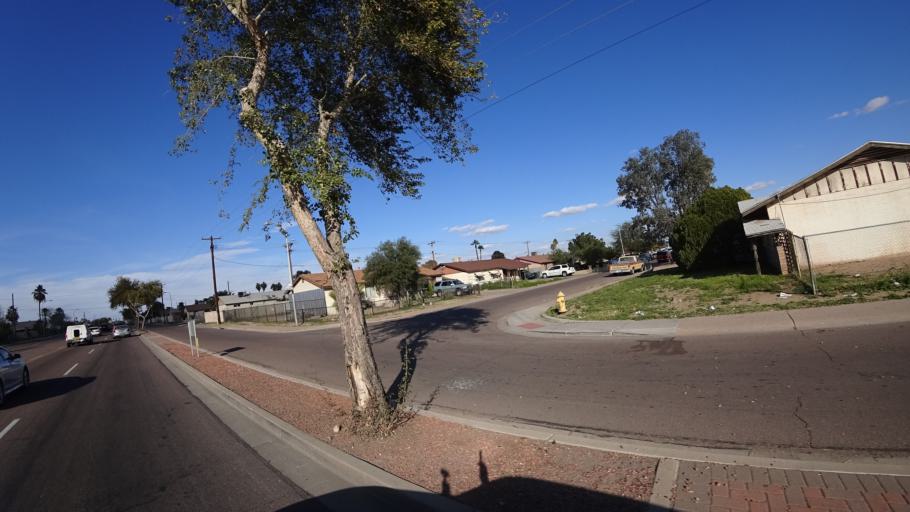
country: US
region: Arizona
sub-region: Maricopa County
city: Tolleson
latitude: 33.4826
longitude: -112.2377
